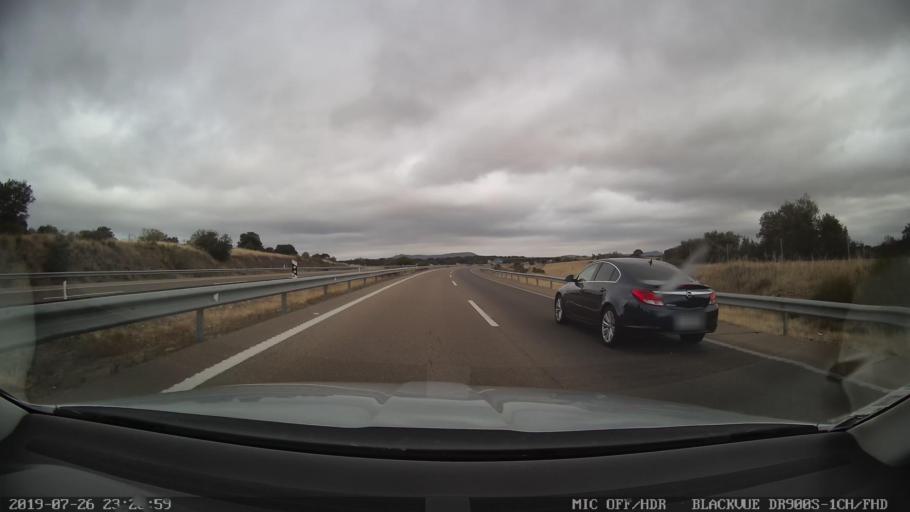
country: ES
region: Extremadura
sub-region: Provincia de Caceres
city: Villamesias
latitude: 39.2175
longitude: -5.8815
